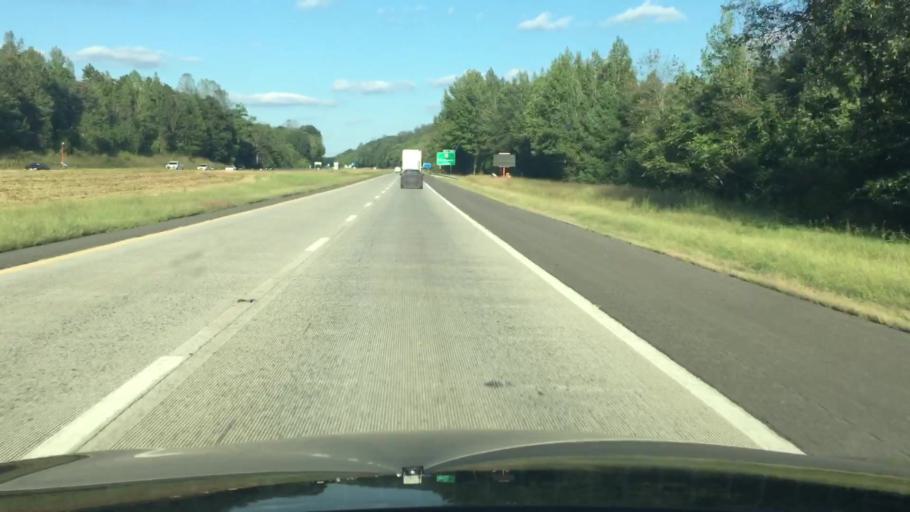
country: US
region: North Carolina
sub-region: Davie County
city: Mocksville
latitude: 35.9009
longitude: -80.6373
